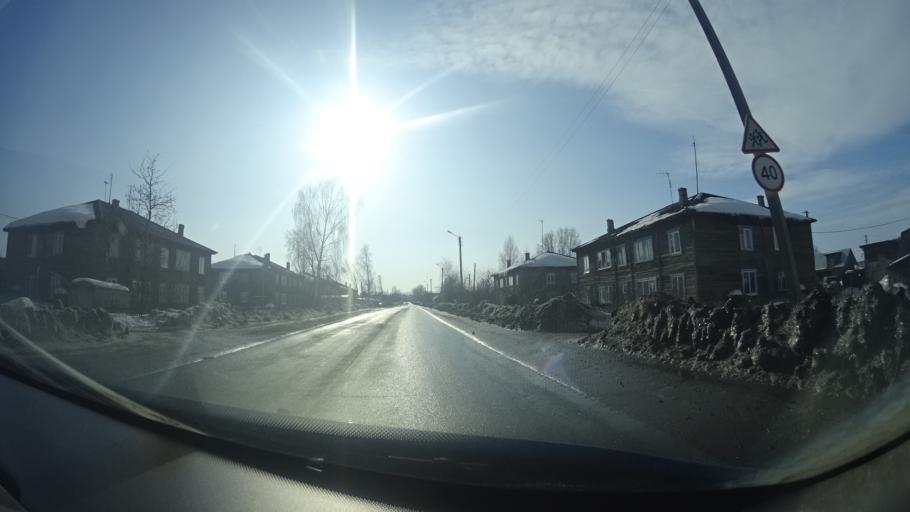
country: RU
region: Perm
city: Kuyeda
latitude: 56.4318
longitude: 55.5757
